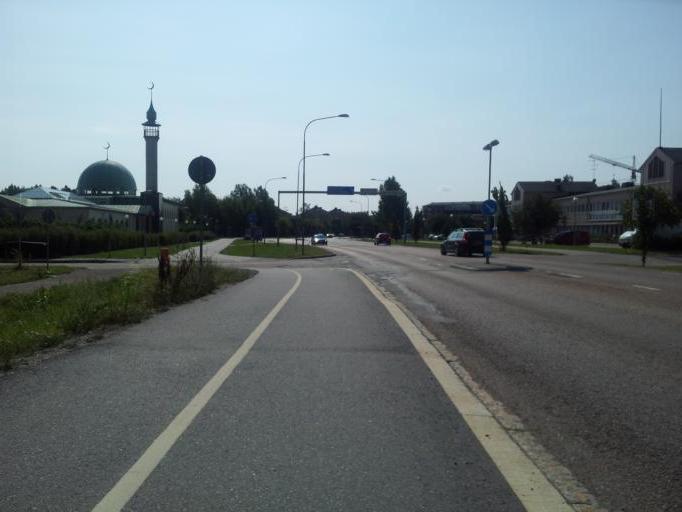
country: SE
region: Uppsala
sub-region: Uppsala Kommun
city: Uppsala
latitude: 59.8746
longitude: 17.6367
